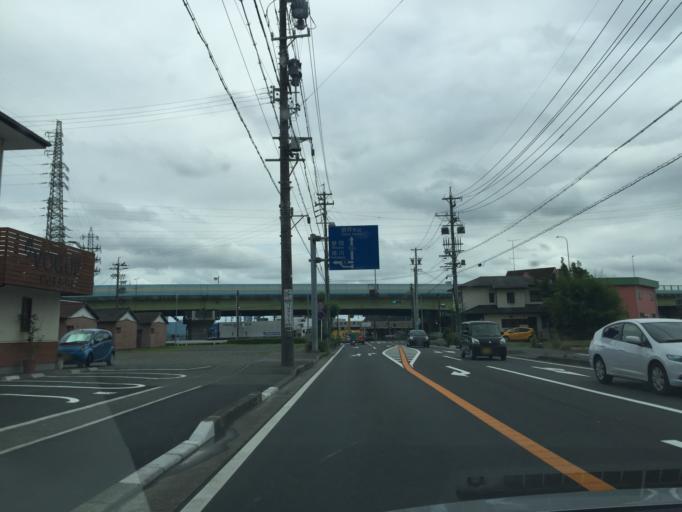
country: JP
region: Shizuoka
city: Fukuroi
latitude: 34.7573
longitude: 137.9184
